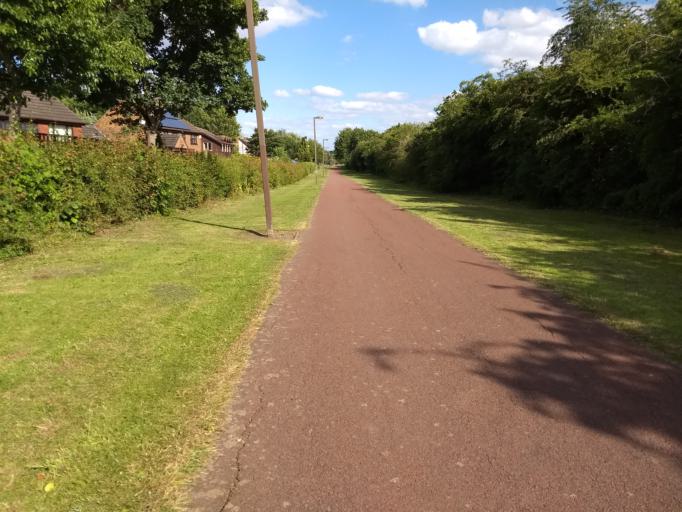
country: GB
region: England
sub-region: Milton Keynes
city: Shenley Church End
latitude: 52.0327
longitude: -0.7996
